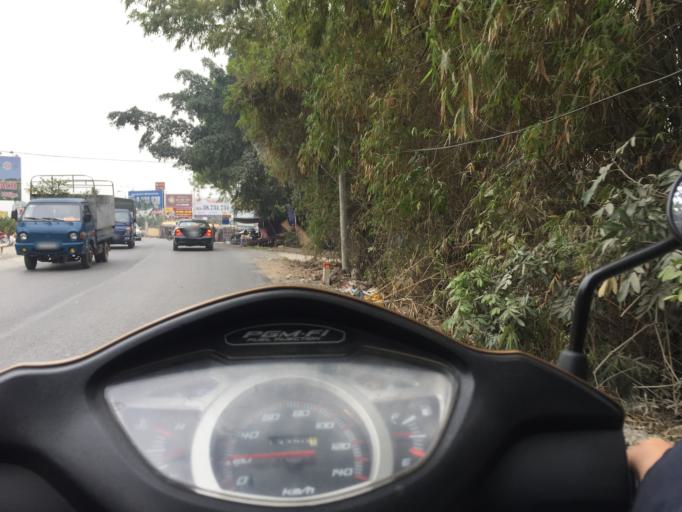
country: VN
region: Hung Yen
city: Van Giang
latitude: 20.9734
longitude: 105.9196
